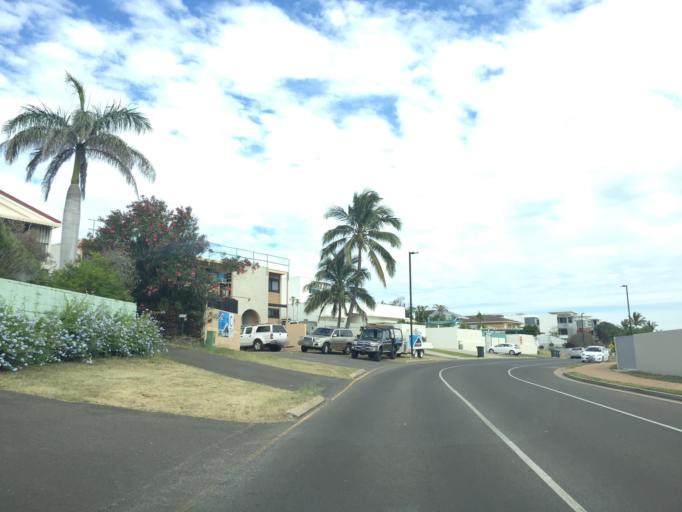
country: AU
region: Queensland
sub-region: Bundaberg
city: Bundaberg
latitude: -24.8215
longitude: 152.4650
